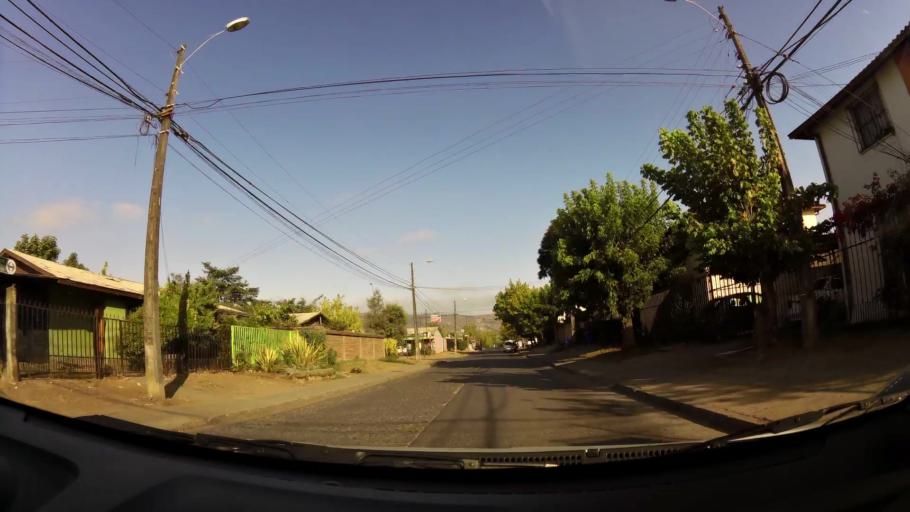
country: CL
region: Maule
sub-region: Provincia de Talca
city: Talca
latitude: -35.4094
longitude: -71.6533
